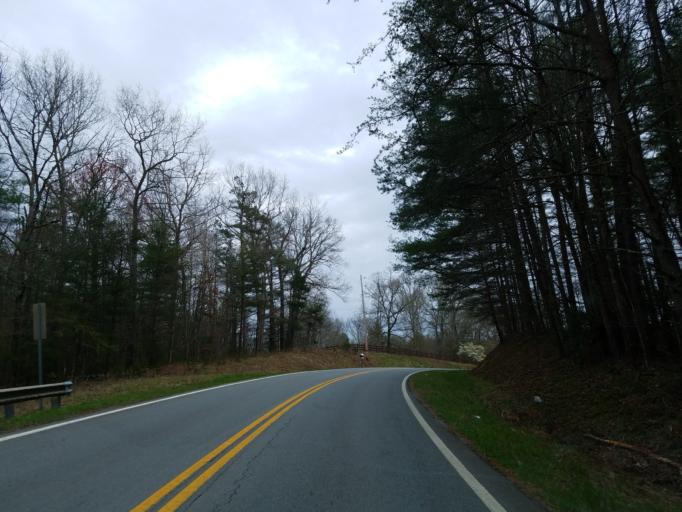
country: US
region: Georgia
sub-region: Fannin County
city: Blue Ridge
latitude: 34.7852
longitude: -84.2471
